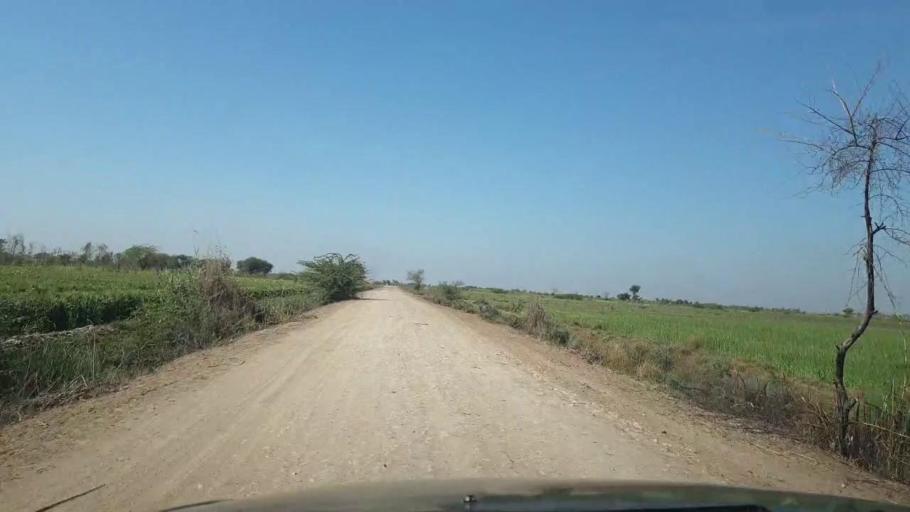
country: PK
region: Sindh
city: Mirpur Khas
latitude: 25.5860
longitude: 69.0620
